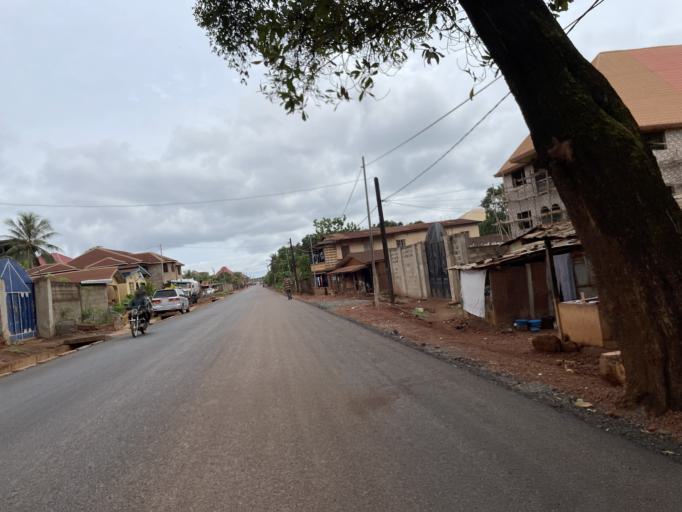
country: SL
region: Western Area
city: Hastings
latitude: 8.4049
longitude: -13.1439
